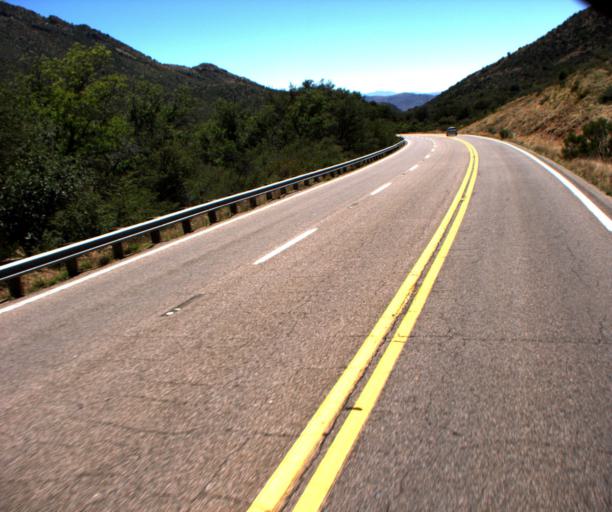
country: US
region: Arizona
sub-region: Gila County
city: Globe
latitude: 33.2315
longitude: -110.7879
